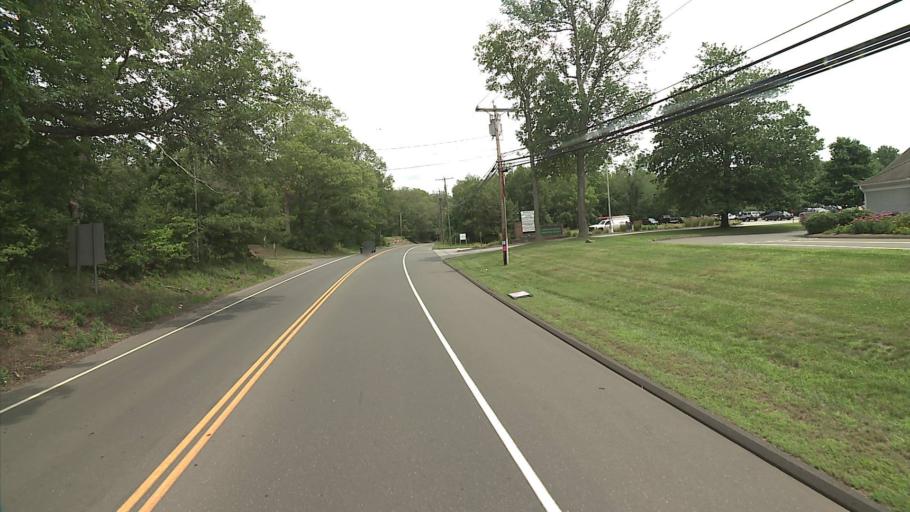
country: US
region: Connecticut
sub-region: New Haven County
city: Guilford
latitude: 41.3605
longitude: -72.6362
